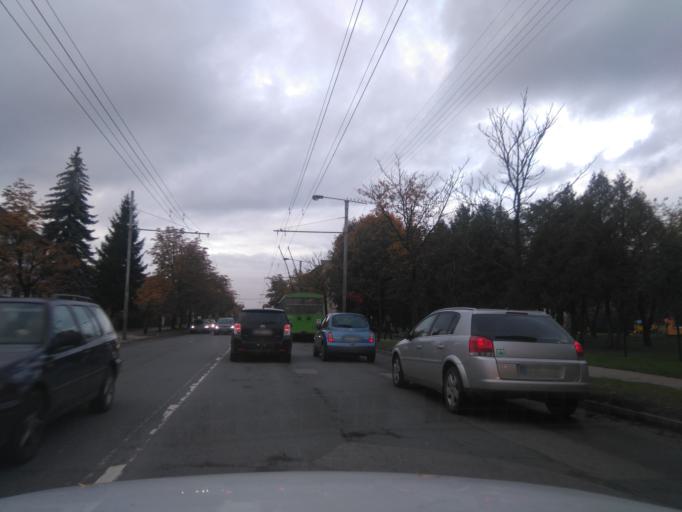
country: LT
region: Kauno apskritis
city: Dainava (Kaunas)
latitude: 54.9036
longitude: 23.9738
